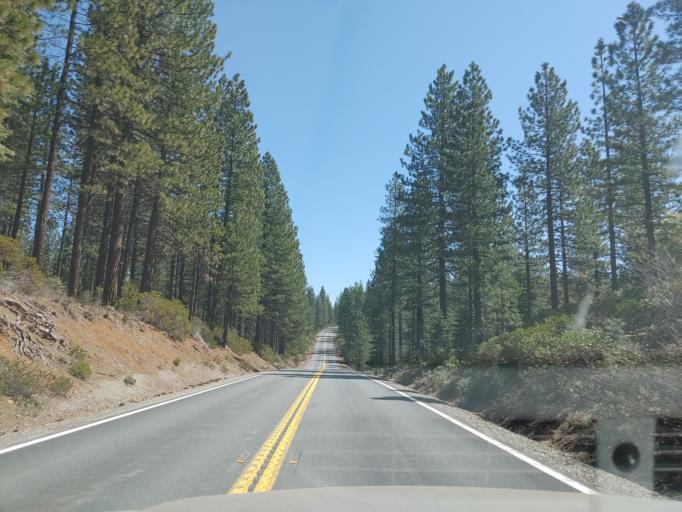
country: US
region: California
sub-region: Siskiyou County
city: McCloud
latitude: 41.2664
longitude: -121.8640
